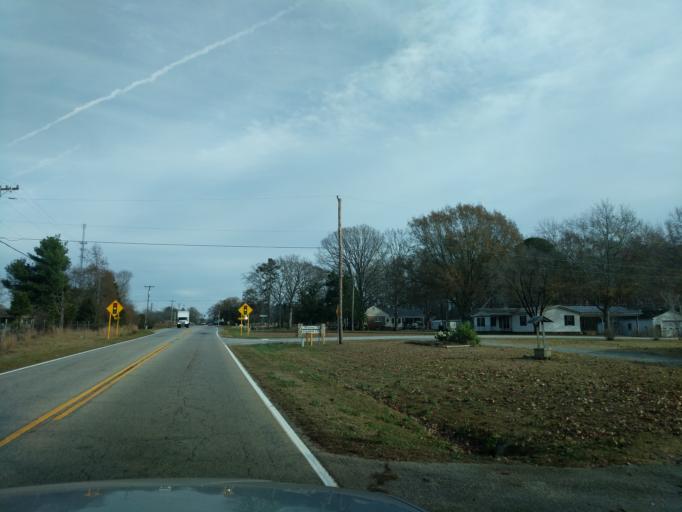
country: US
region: South Carolina
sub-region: Anderson County
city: Powdersville
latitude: 34.7185
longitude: -82.5781
